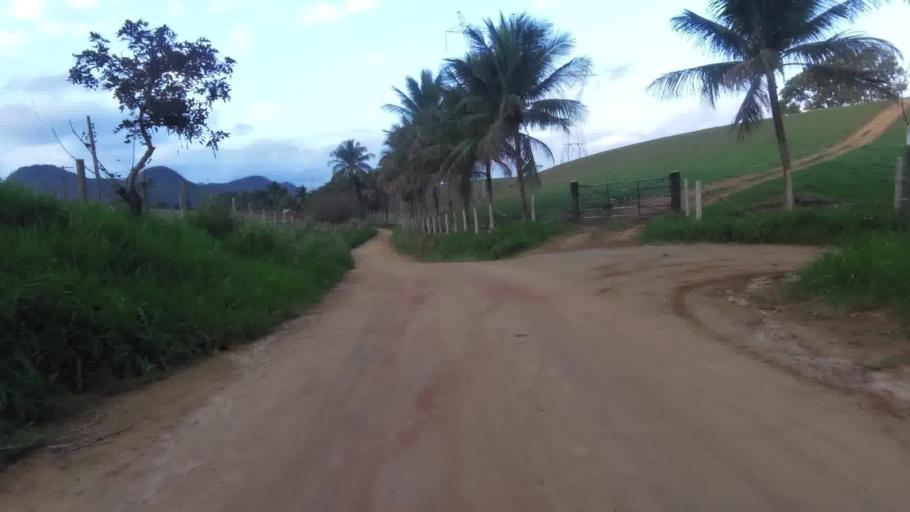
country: BR
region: Espirito Santo
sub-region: Guarapari
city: Guarapari
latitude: -20.6780
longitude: -40.6201
